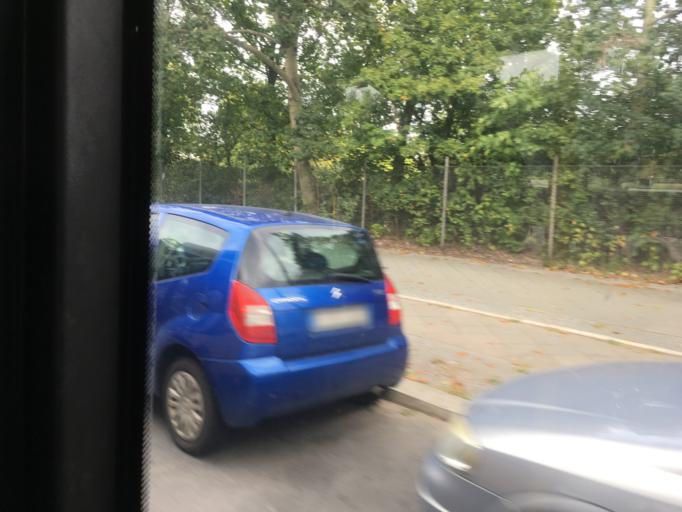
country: DE
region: Berlin
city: Wilhelmstadt
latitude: 52.5176
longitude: 13.1865
